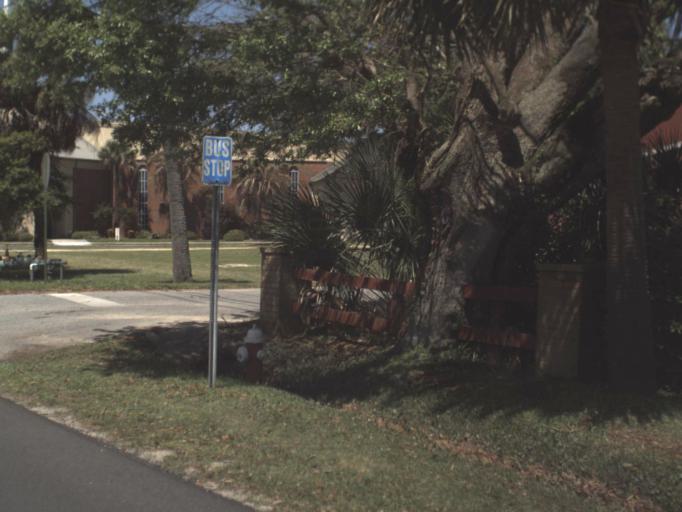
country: US
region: Florida
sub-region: Escambia County
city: West Pensacola
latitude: 30.4250
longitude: -87.2938
